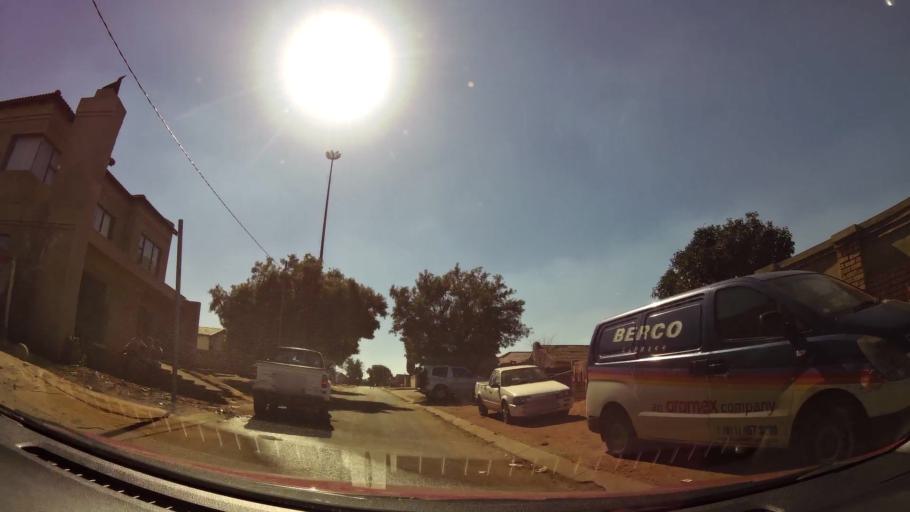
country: ZA
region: Gauteng
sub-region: City of Johannesburg Metropolitan Municipality
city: Soweto
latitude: -26.2510
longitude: 27.8062
